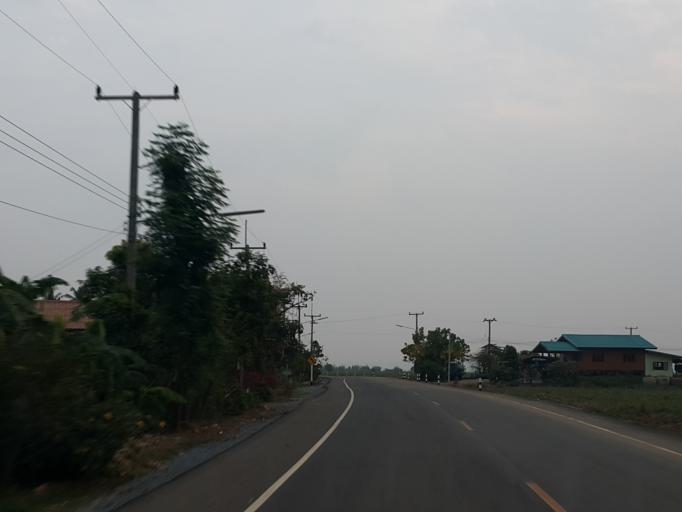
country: TH
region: Suphan Buri
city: Dan Chang
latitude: 14.9352
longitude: 99.6407
